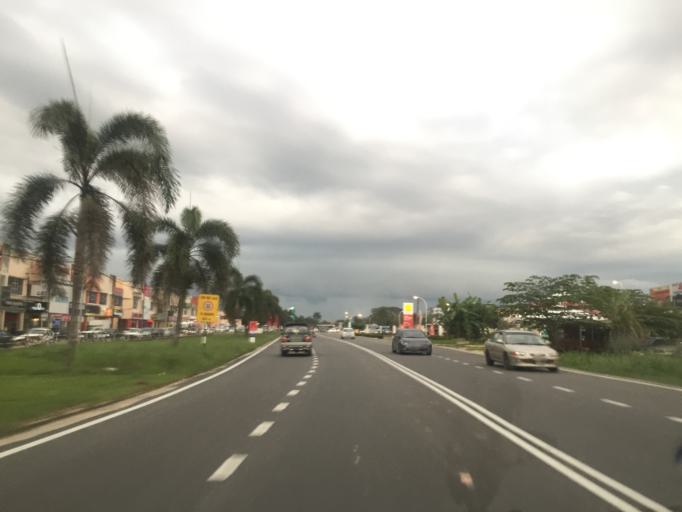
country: MY
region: Penang
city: Tasek Glugor
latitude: 5.5151
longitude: 100.5435
